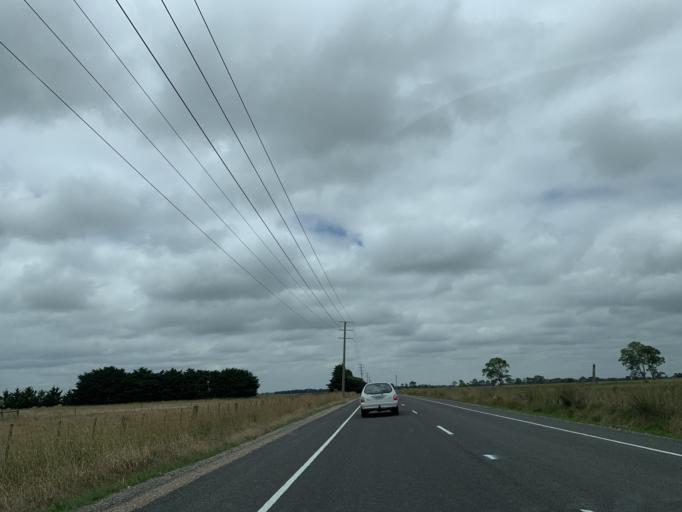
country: AU
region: Victoria
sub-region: Wellington
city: Heyfield
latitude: -37.9881
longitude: 146.8614
